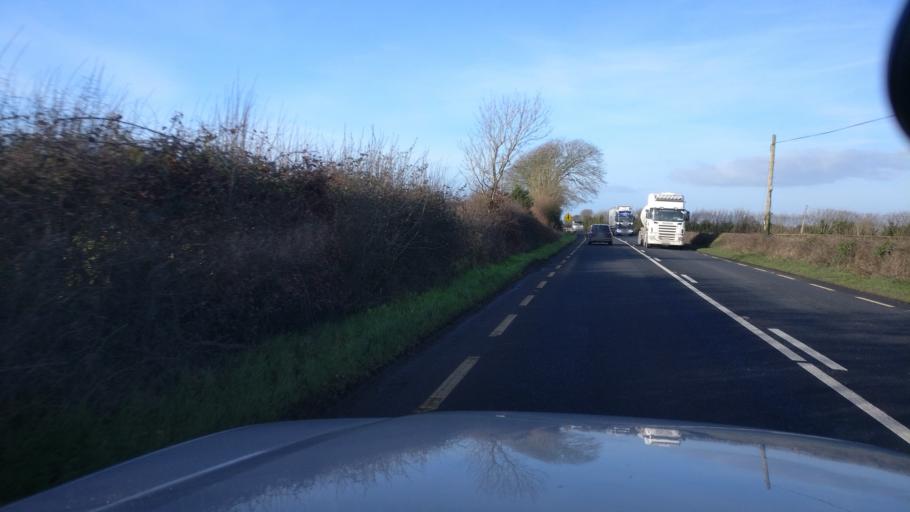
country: IE
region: Leinster
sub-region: Uibh Fhaili
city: Tullamore
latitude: 53.2042
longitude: -7.4337
